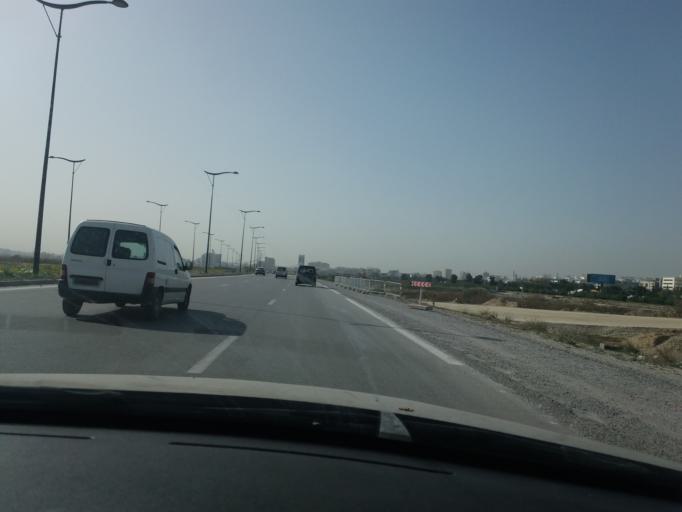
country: TN
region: Tunis
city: Tunis
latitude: 36.8219
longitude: 10.2016
